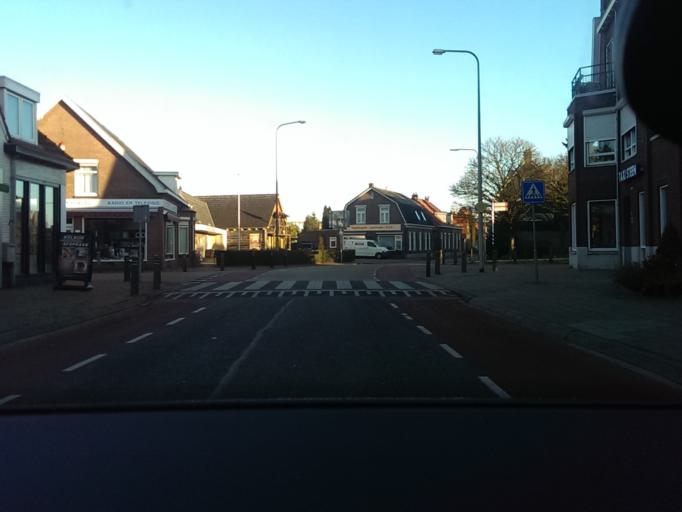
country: NL
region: Overijssel
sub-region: Gemeente Twenterand
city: Den Ham
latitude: 52.5202
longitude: 6.4255
